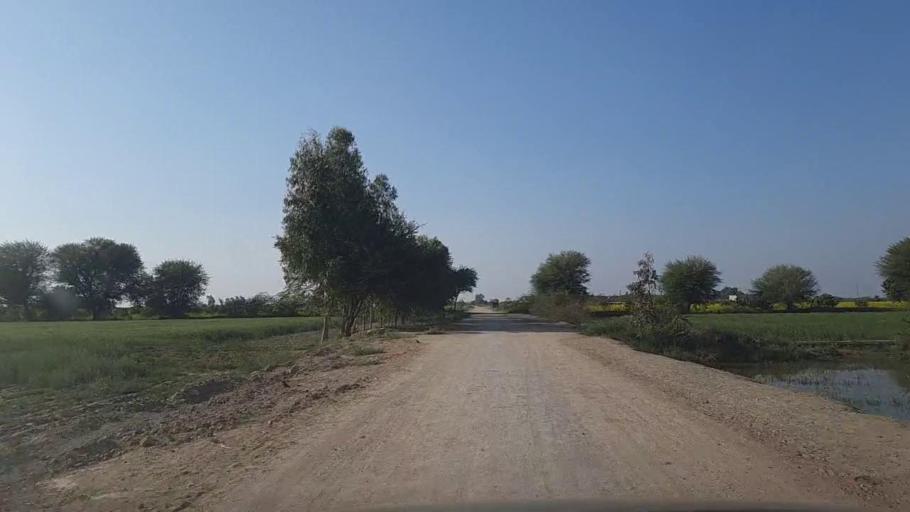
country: PK
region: Sindh
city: Digri
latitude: 25.0262
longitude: 69.2261
